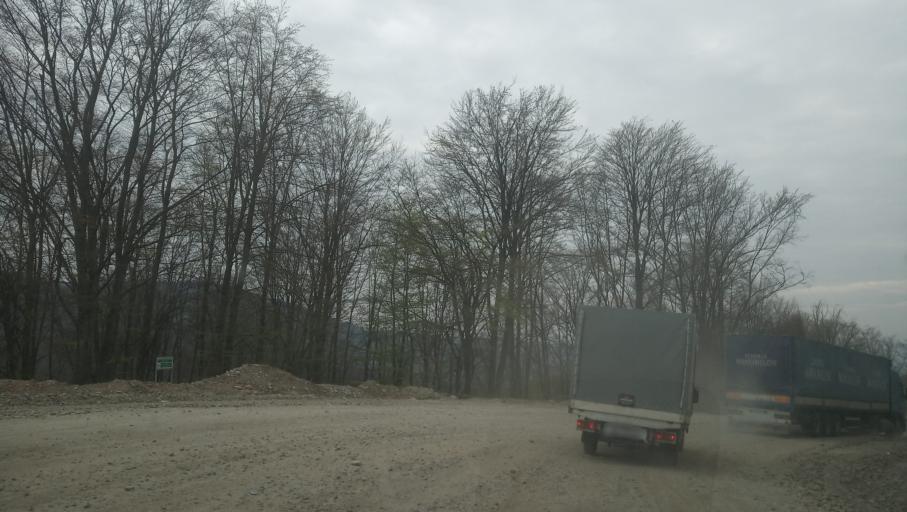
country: RO
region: Arad
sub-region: Comuna Varfurile
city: Varfurile
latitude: 46.3707
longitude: 22.5542
